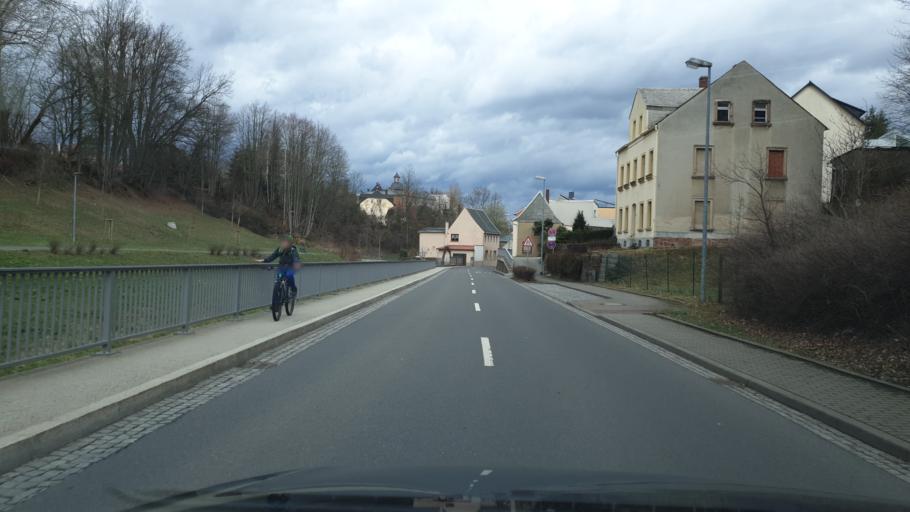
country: DE
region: Saxony
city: Mittweida
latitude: 50.9804
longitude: 12.9755
